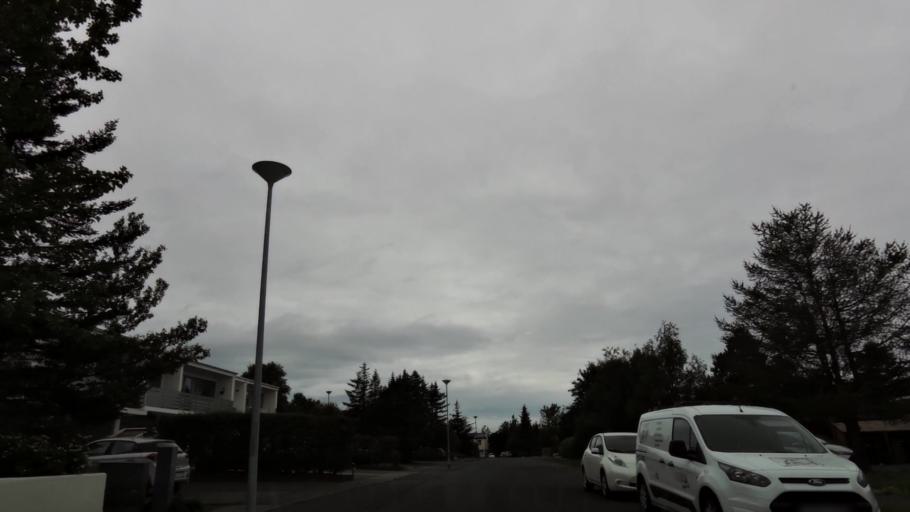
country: IS
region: Capital Region
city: Gardabaer
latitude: 64.0897
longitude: -21.8997
